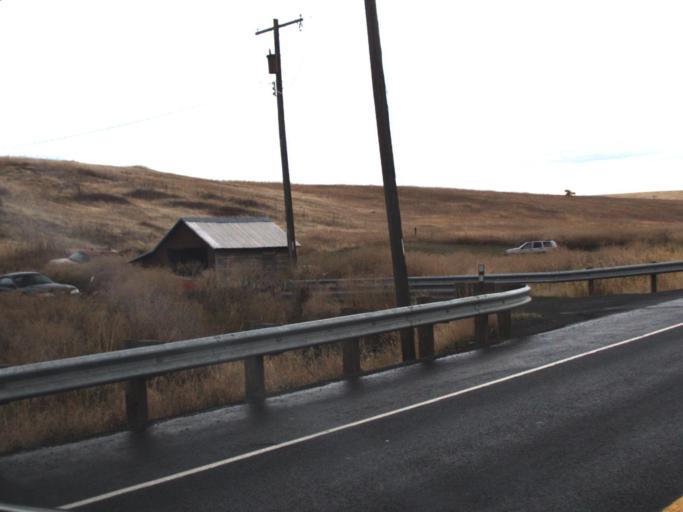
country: US
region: Washington
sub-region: Asotin County
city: Clarkston
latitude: 46.5343
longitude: -117.0861
